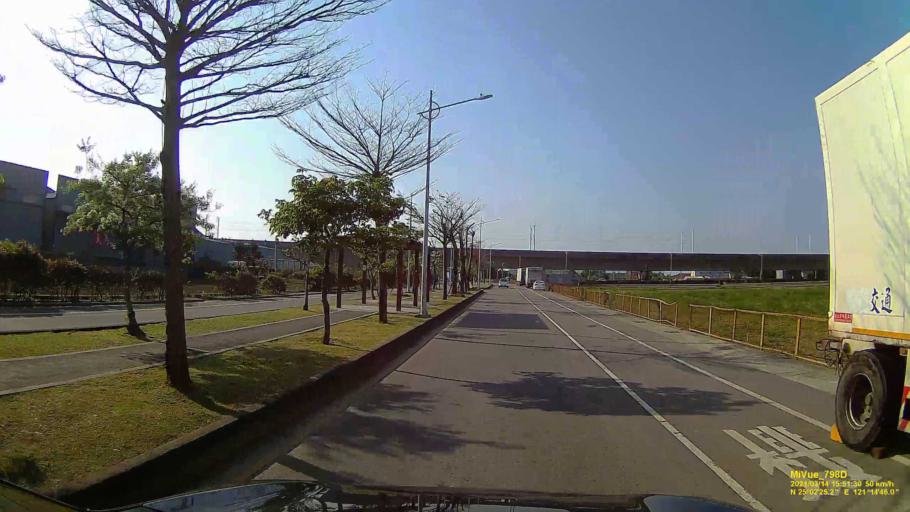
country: TW
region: Taiwan
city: Taoyuan City
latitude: 25.0405
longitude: 121.2459
